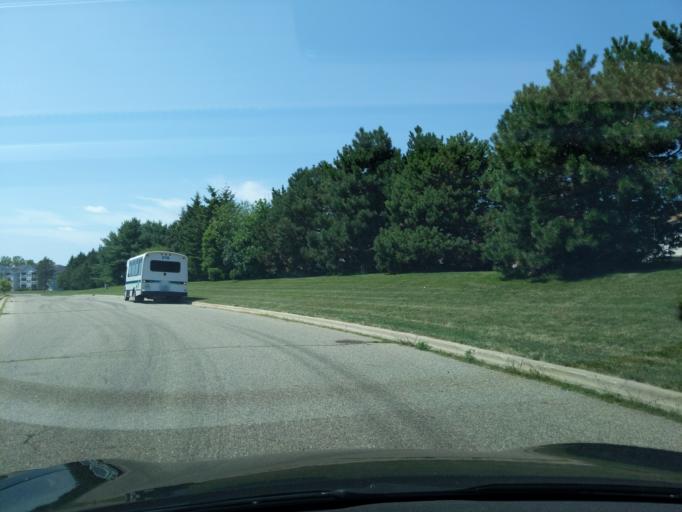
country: US
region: Michigan
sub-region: Eaton County
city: Waverly
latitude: 42.7450
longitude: -84.6443
